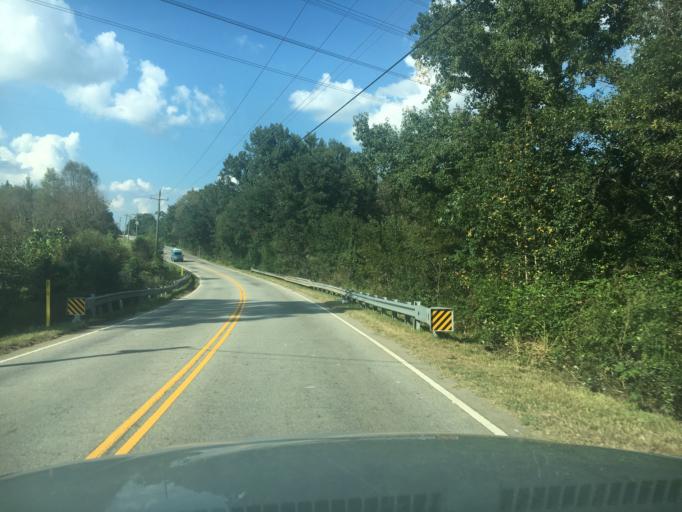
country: US
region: South Carolina
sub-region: Greenville County
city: Simpsonville
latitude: 34.6864
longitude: -82.2522
